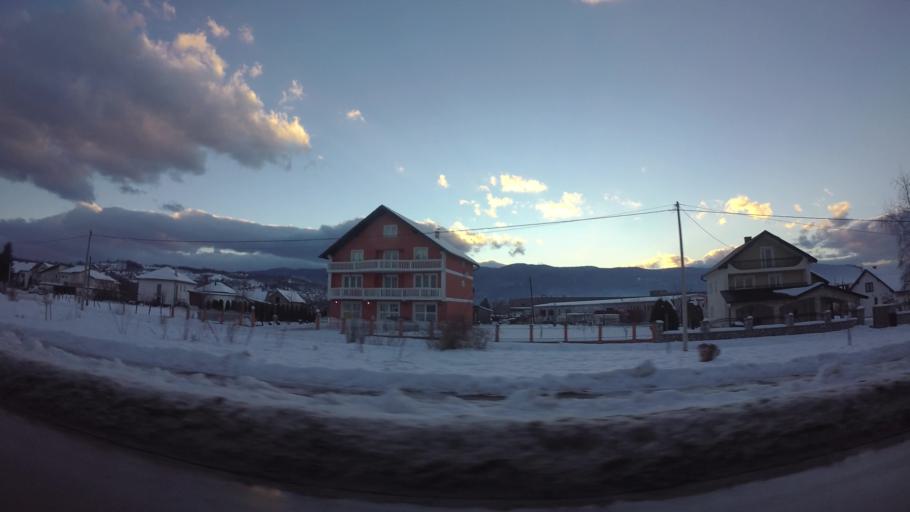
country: BA
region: Federation of Bosnia and Herzegovina
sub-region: Kanton Sarajevo
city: Sarajevo
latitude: 43.8175
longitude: 18.3593
